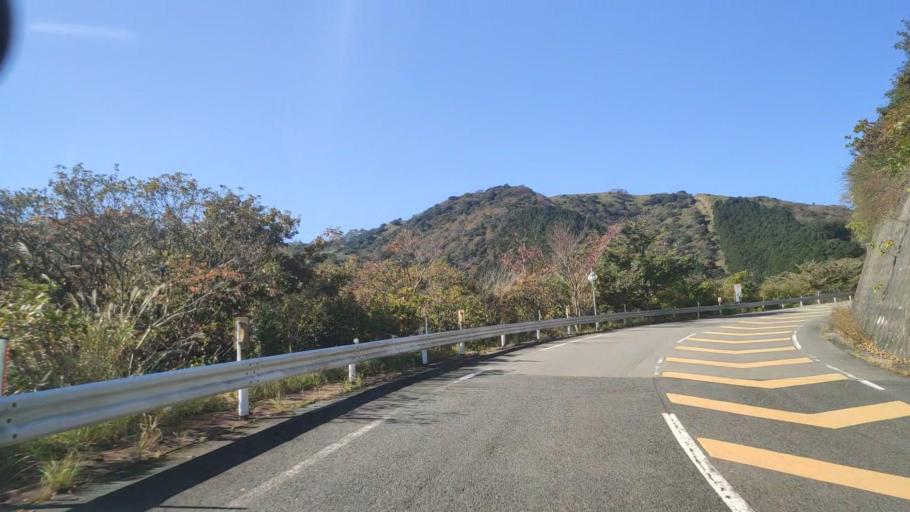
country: JP
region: Shizuoka
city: Atami
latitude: 35.0468
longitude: 139.0397
